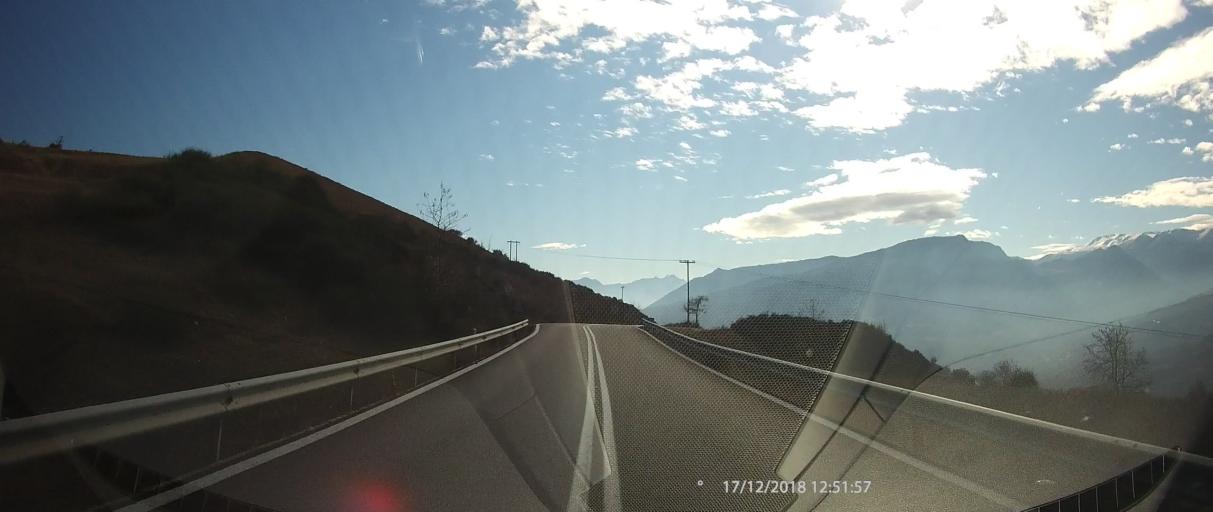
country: GR
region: Thessaly
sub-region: Trikala
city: Kastraki
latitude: 39.7607
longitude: 21.4738
